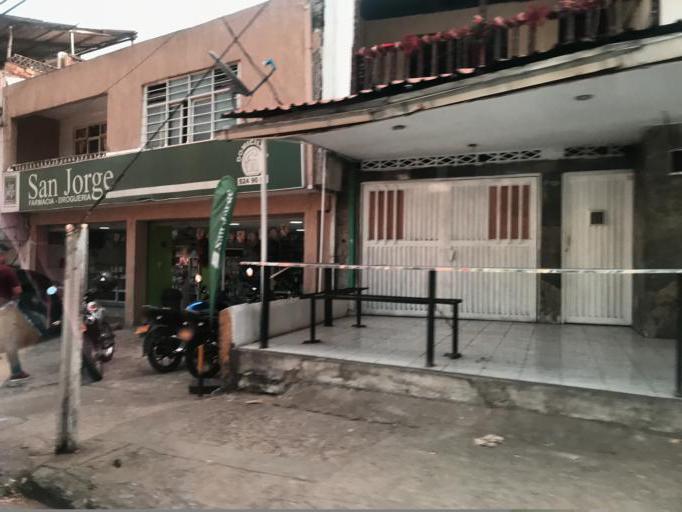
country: CO
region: Valle del Cauca
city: Cali
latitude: 3.4538
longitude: -76.5506
